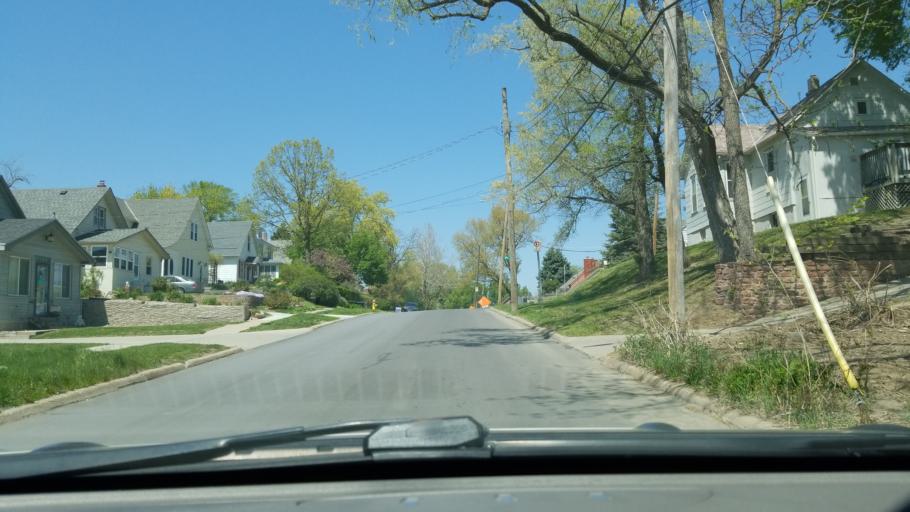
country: US
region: Nebraska
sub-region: Douglas County
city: Omaha
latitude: 41.2236
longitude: -95.9374
